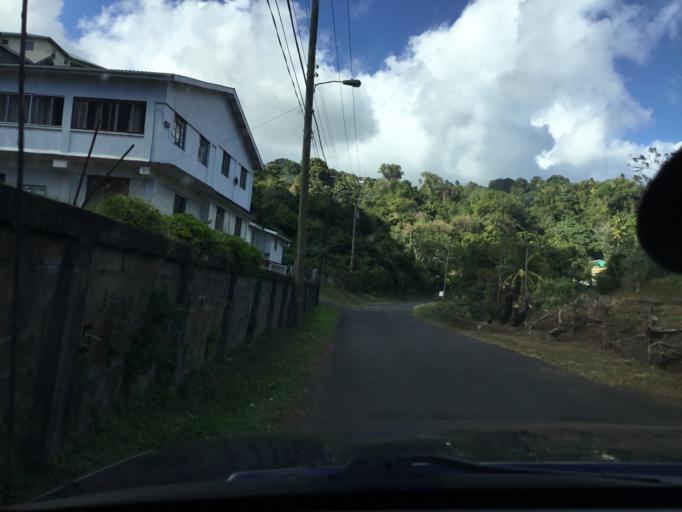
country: VC
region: Saint George
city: Kingstown
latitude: 13.1461
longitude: -61.1750
